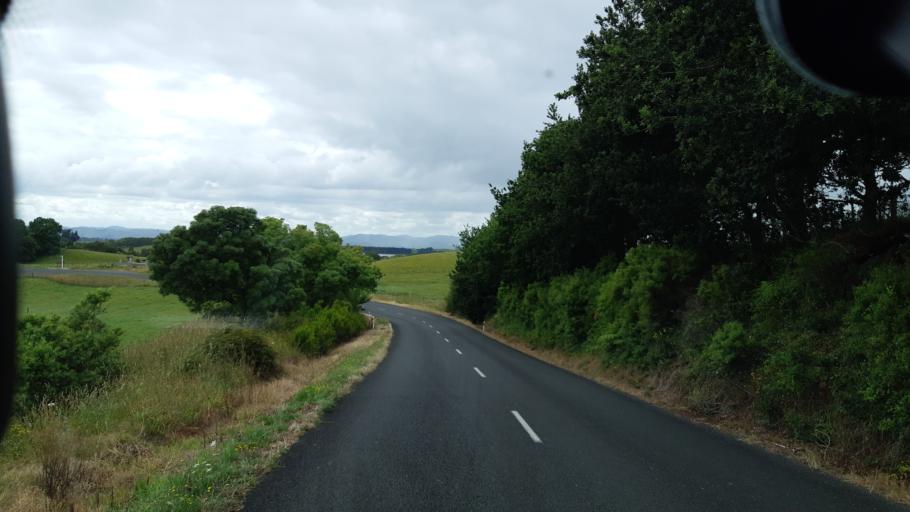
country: NZ
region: Waikato
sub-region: Waikato District
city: Te Kauwhata
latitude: -37.4882
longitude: 175.0940
